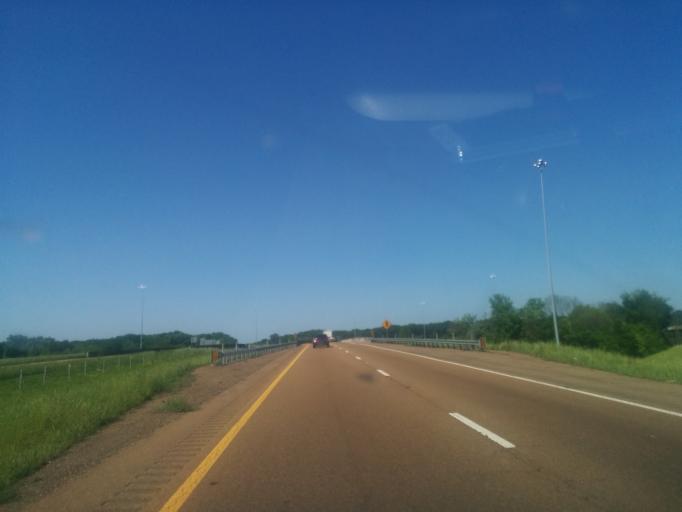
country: US
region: Mississippi
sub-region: Hinds County
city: Jackson
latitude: 32.3247
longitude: -90.2473
